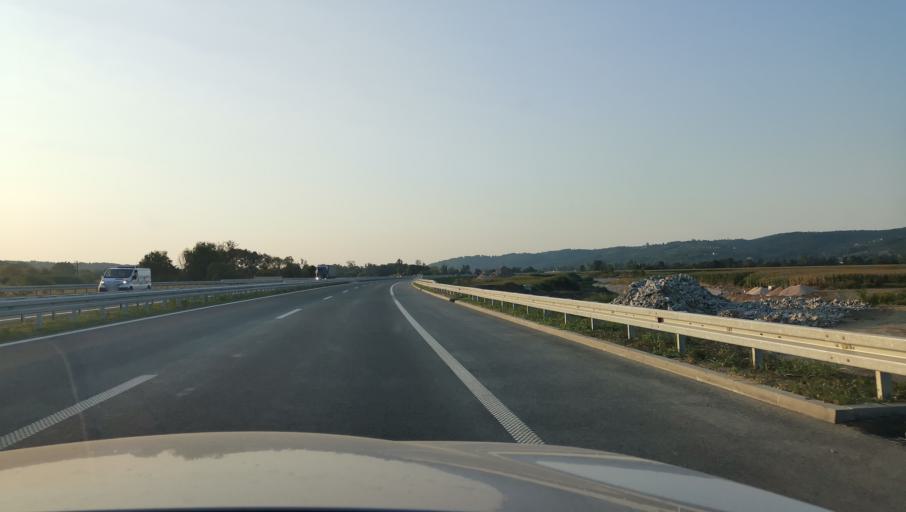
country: RS
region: Central Serbia
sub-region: Kolubarski Okrug
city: Lajkovac
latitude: 44.3155
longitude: 20.2154
